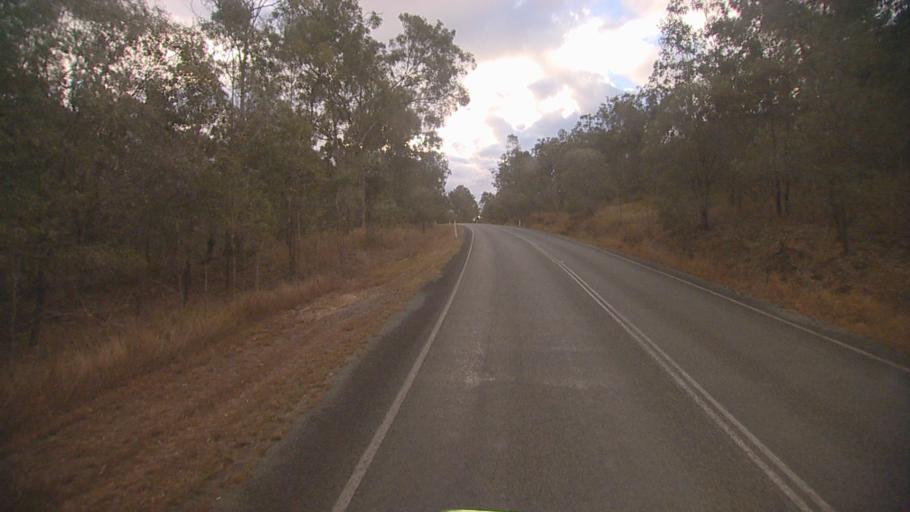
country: AU
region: Queensland
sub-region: Logan
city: Cedar Vale
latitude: -27.8919
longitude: 153.0856
